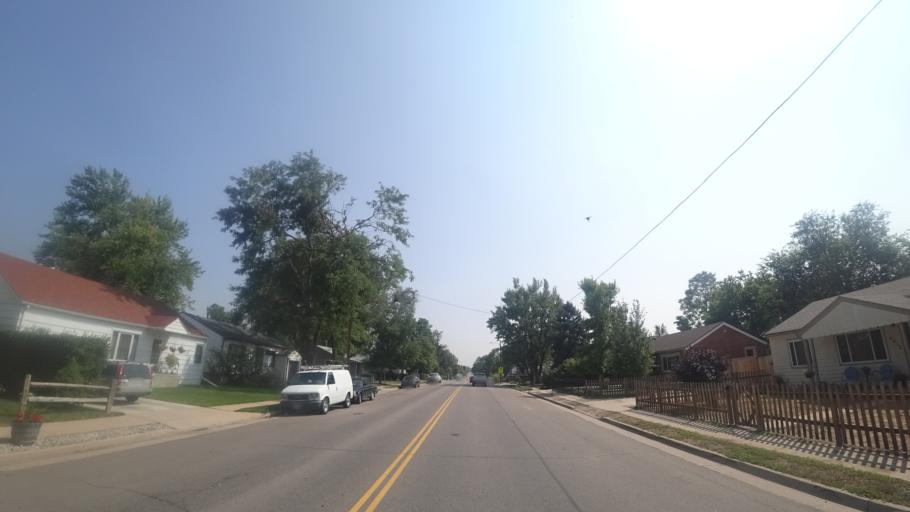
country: US
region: Colorado
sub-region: Arapahoe County
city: Englewood
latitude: 39.6347
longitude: -104.9832
